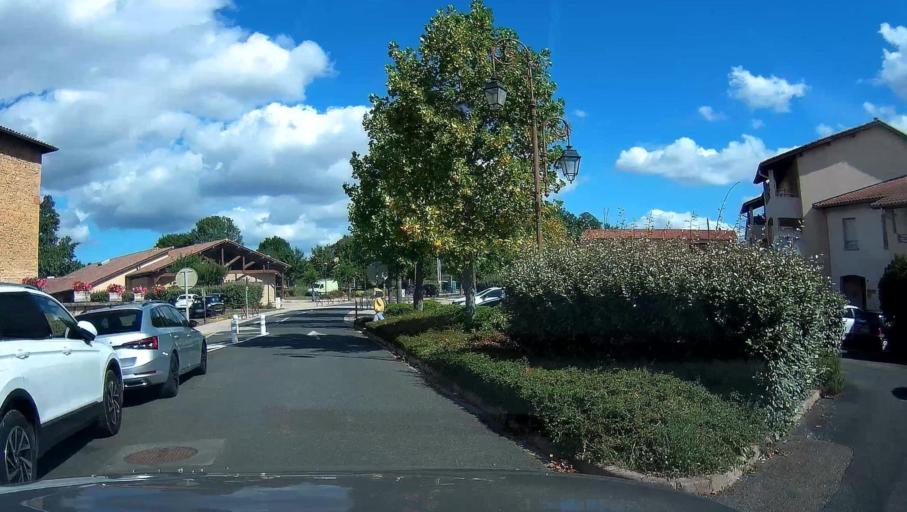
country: FR
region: Rhone-Alpes
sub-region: Departement du Rhone
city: Liergues
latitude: 45.9704
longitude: 4.6641
